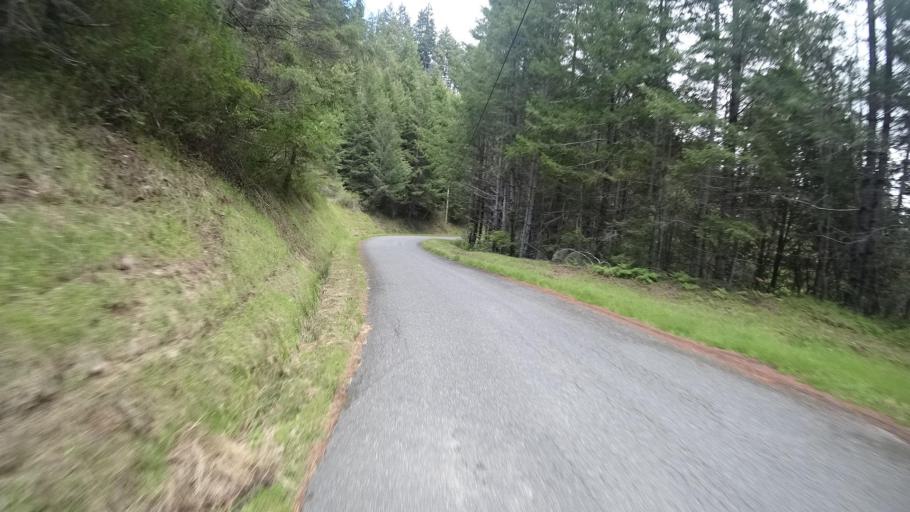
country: US
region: California
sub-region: Humboldt County
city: Blue Lake
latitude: 40.7629
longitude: -123.9237
